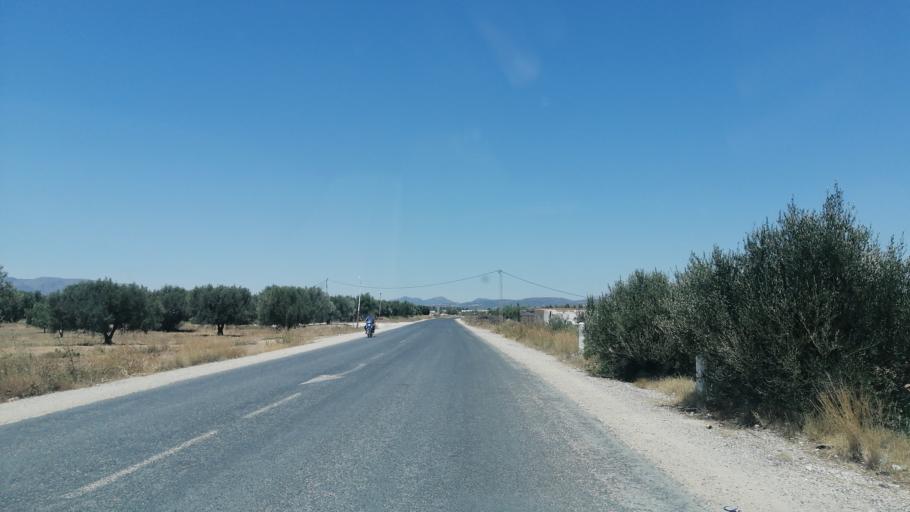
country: TN
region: Al Qayrawan
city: Sbikha
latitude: 36.1311
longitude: 10.0919
